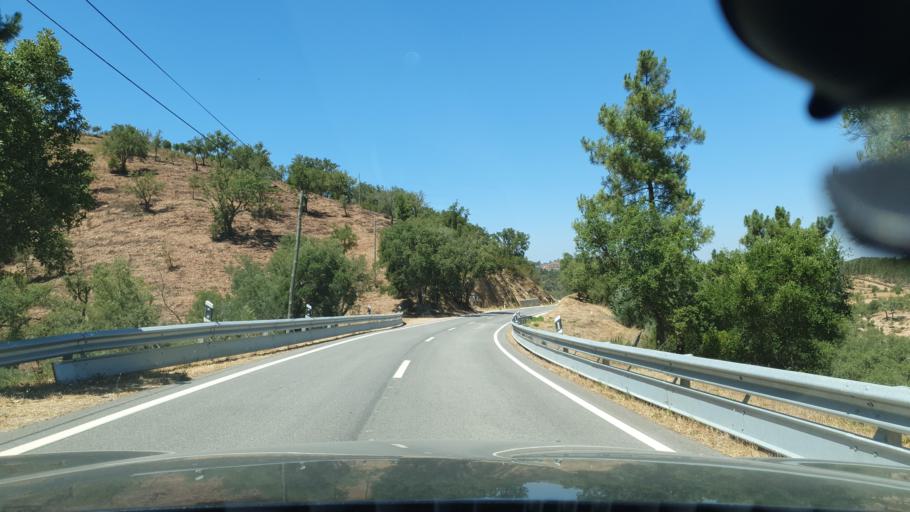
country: PT
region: Beja
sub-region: Odemira
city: Odemira
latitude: 37.5346
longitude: -8.4817
